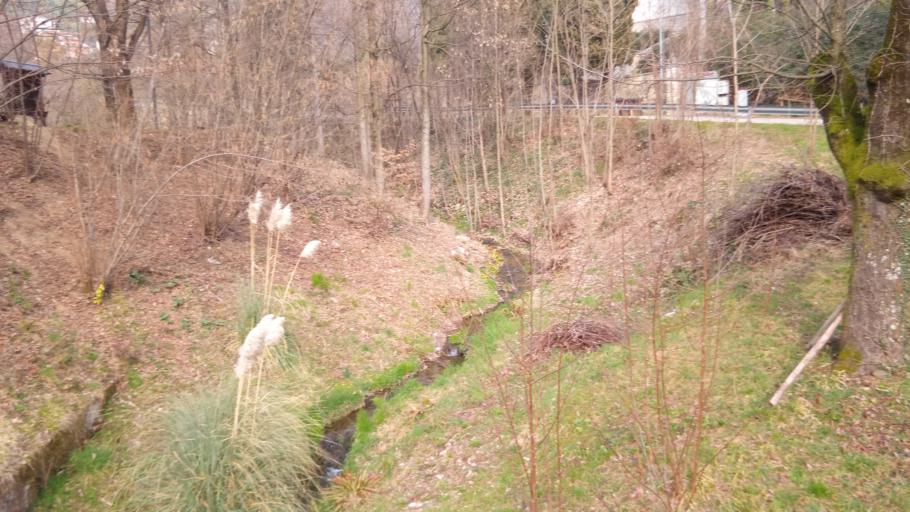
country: IT
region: Veneto
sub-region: Provincia di Vicenza
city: Campese
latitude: 45.7864
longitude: 11.6923
